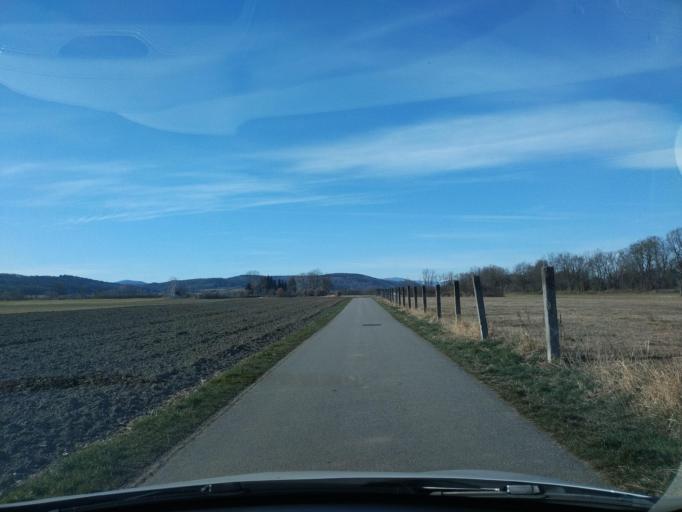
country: AT
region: Lower Austria
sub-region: Politischer Bezirk Wiener Neustadt
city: Lanzenkirchen
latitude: 47.7397
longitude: 16.2419
